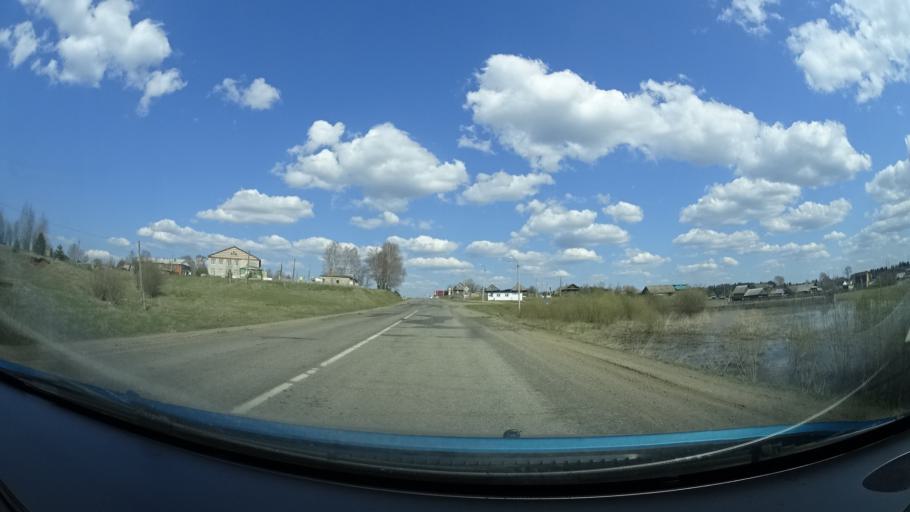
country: RU
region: Perm
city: Yugo-Kamskiy
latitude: 57.4520
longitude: 55.6559
